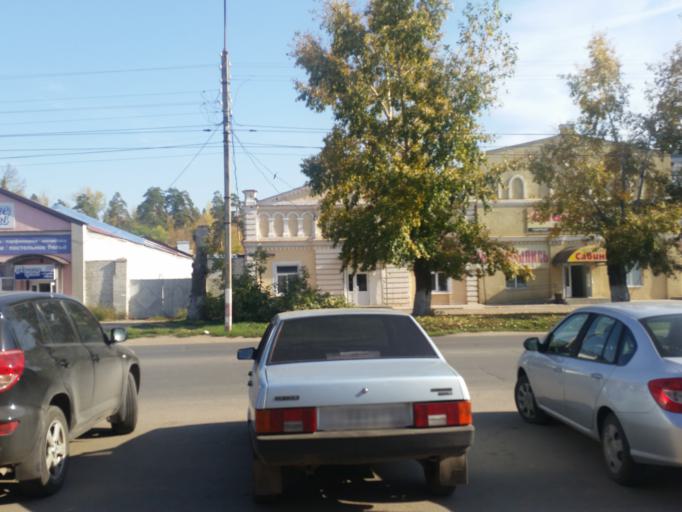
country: RU
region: Ulyanovsk
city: Dimitrovgrad
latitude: 54.2260
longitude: 49.6143
